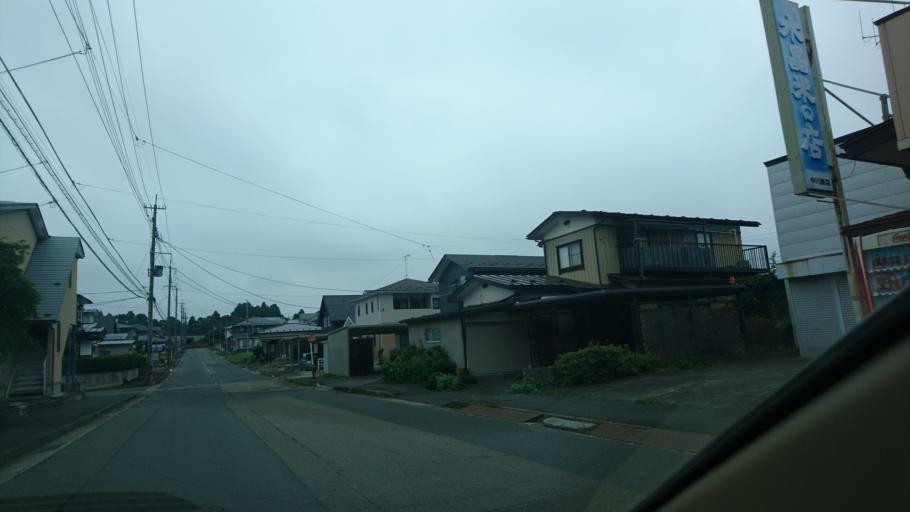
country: JP
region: Iwate
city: Kitakami
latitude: 39.2631
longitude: 141.1065
